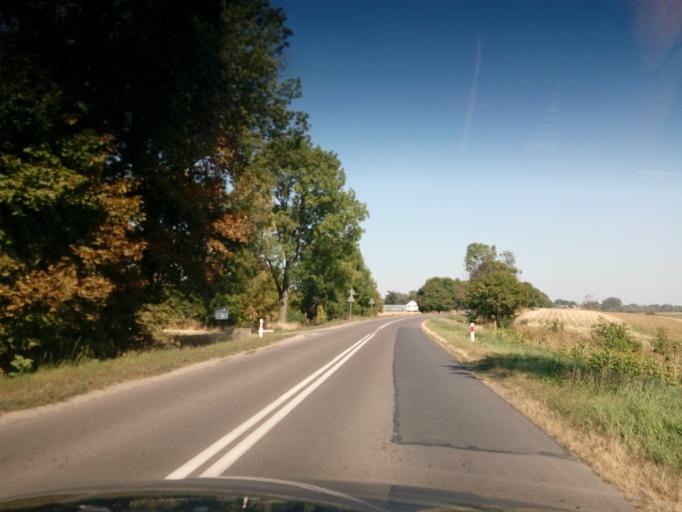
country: PL
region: Lublin Voivodeship
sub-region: Powiat hrubieszowski
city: Hrubieszow
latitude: 50.8295
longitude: 23.9579
